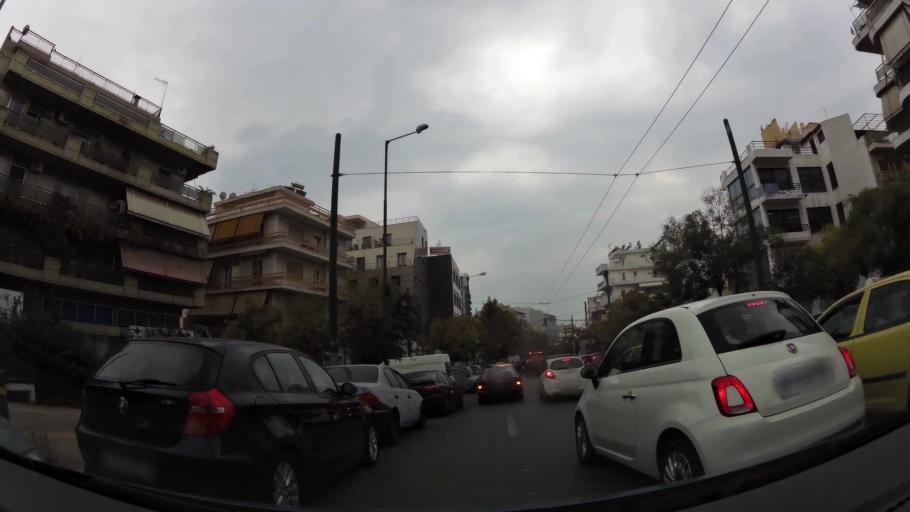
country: GR
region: Attica
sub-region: Nomarchia Athinas
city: Dhafni
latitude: 37.9598
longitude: 23.7364
